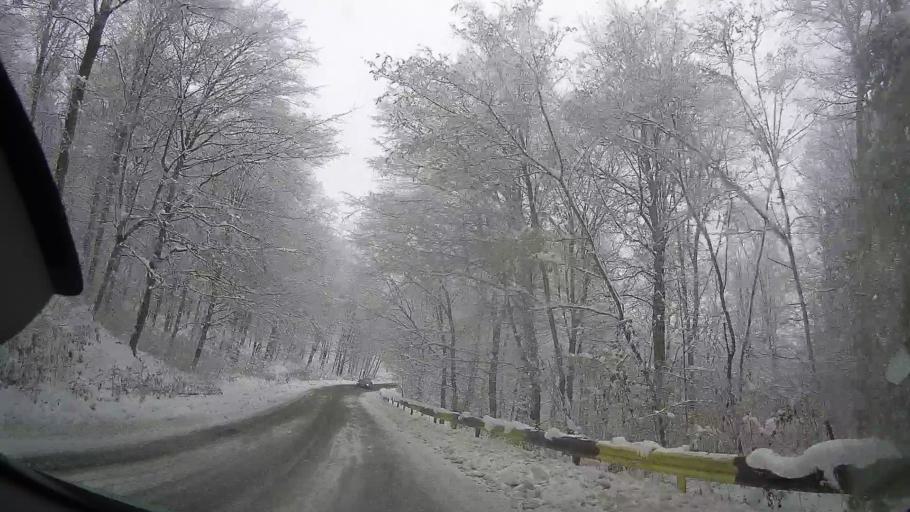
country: RO
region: Neamt
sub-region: Comuna Valea Ursului
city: Valea Ursului
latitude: 46.8453
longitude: 27.0671
